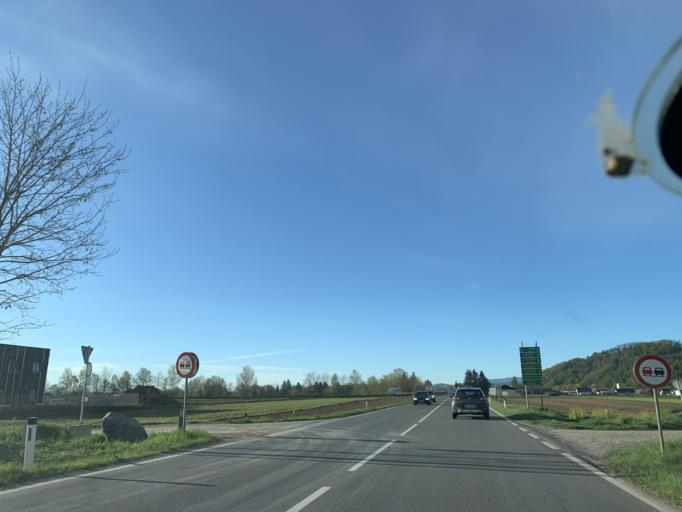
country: AT
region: Styria
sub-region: Politischer Bezirk Leibnitz
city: Kaindorf an der Sulm
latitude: 46.8150
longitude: 15.5261
